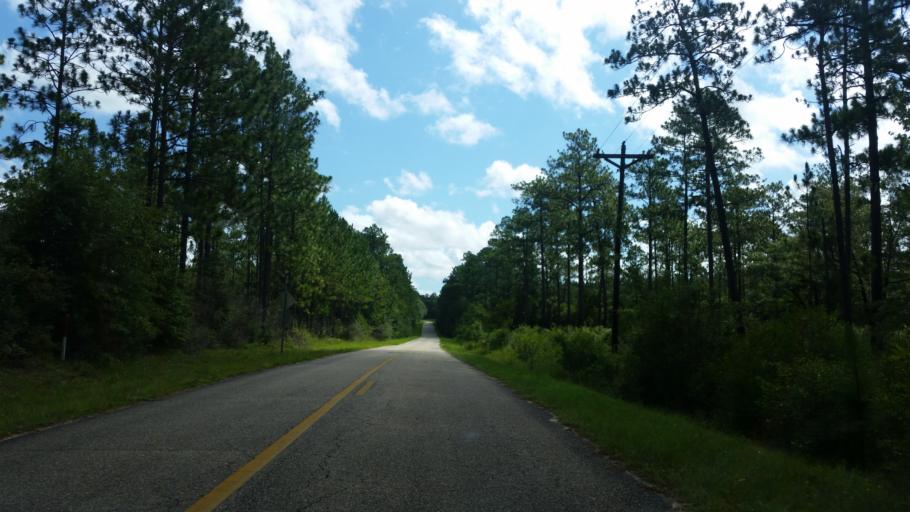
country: US
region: Florida
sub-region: Santa Rosa County
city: Point Baker
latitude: 30.7277
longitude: -86.8975
